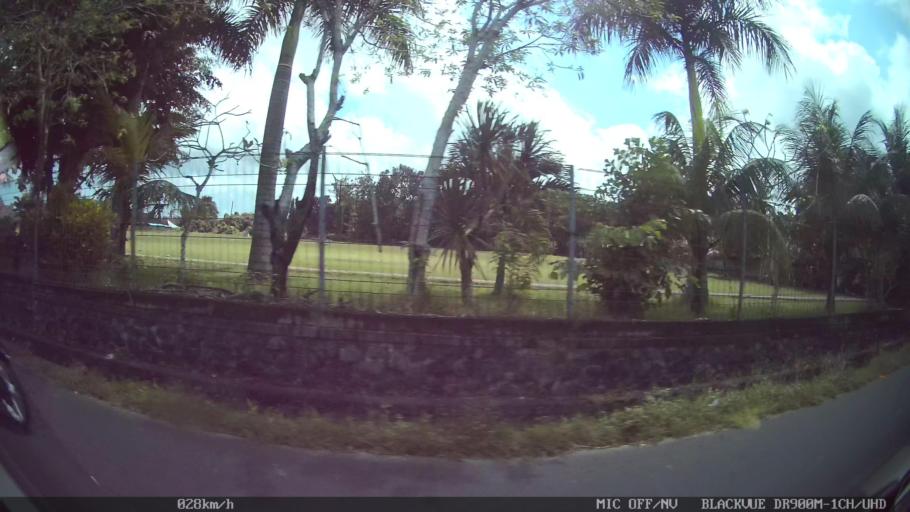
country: ID
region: Bali
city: Klungkung
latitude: -8.5201
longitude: 115.3798
